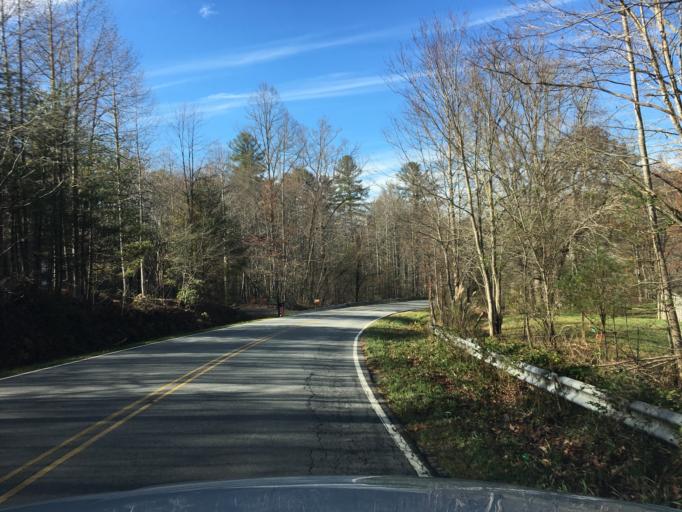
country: US
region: North Carolina
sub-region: Henderson County
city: Etowah
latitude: 35.2315
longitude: -82.5985
